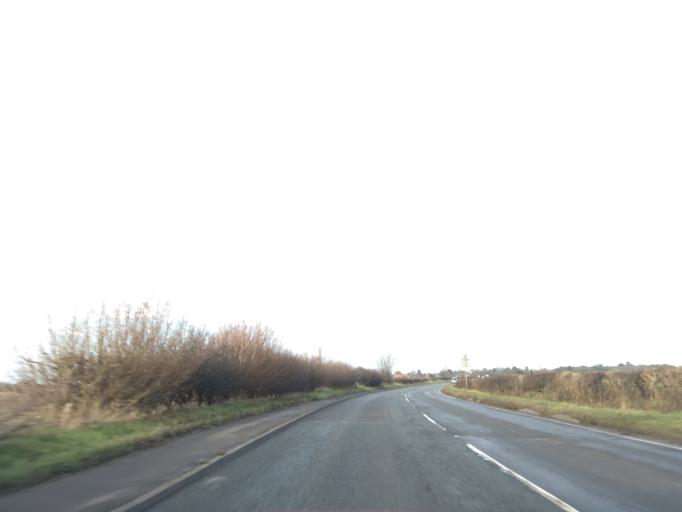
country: GB
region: England
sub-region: Nottinghamshire
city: South Collingham
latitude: 53.1647
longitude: -0.7655
